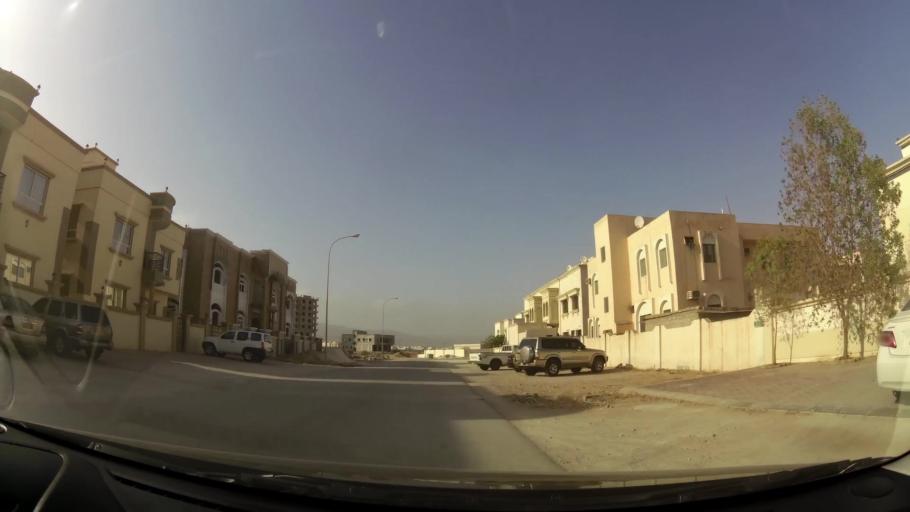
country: OM
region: Zufar
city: Salalah
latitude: 17.0235
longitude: 54.0229
